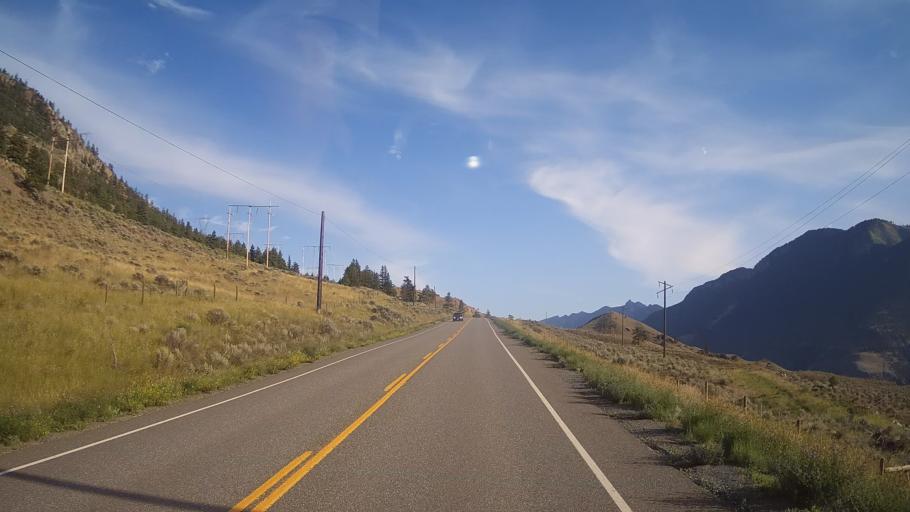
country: CA
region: British Columbia
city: Lillooet
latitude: 50.8338
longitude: -121.8607
